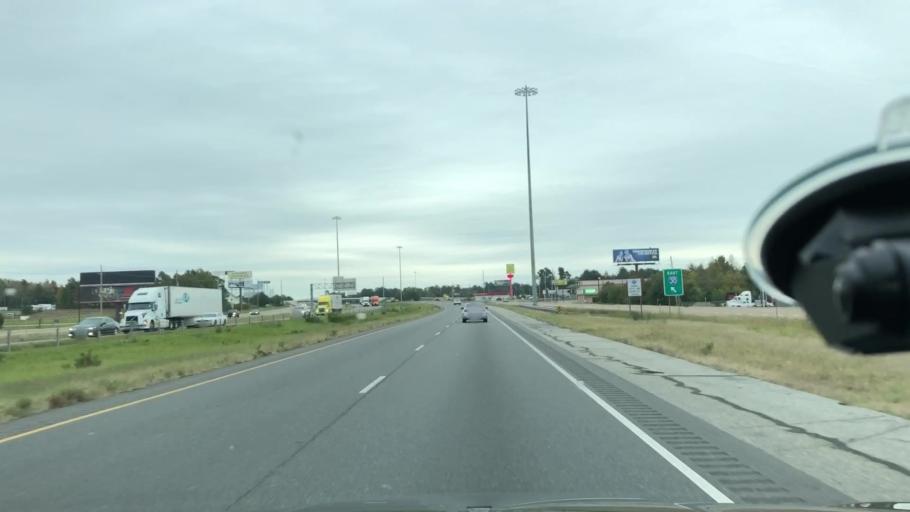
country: US
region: Arkansas
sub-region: Miller County
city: Texarkana
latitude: 33.4701
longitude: -94.0379
